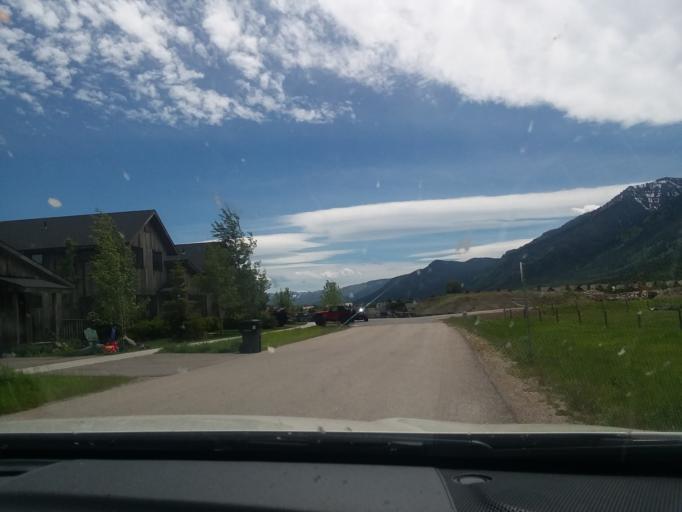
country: US
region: Wyoming
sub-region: Teton County
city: Moose Wilson Road
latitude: 43.5869
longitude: -110.8229
